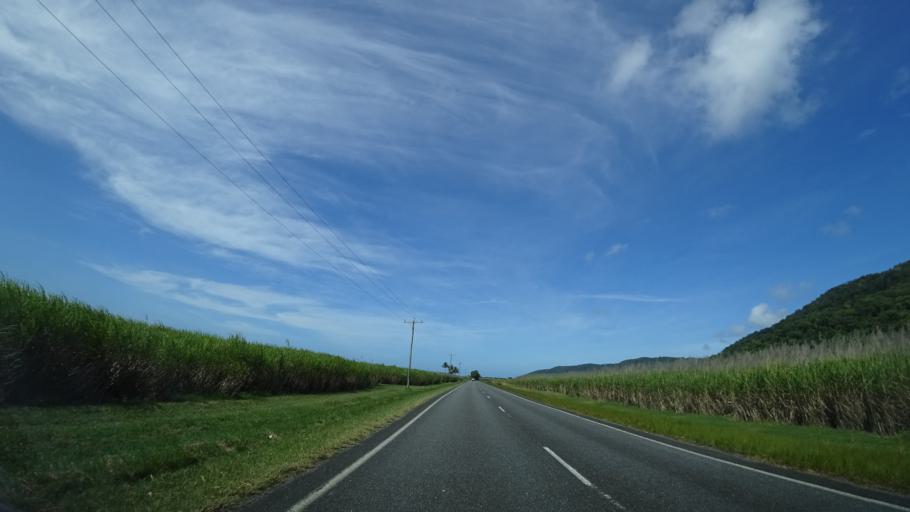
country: AU
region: Queensland
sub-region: Cairns
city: Port Douglas
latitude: -16.2888
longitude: 145.3845
